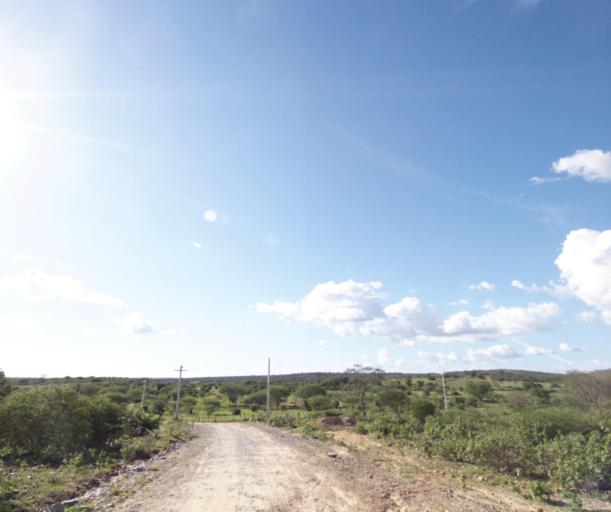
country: BR
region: Bahia
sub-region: Tanhacu
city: Tanhacu
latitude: -14.1816
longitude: -41.0023
